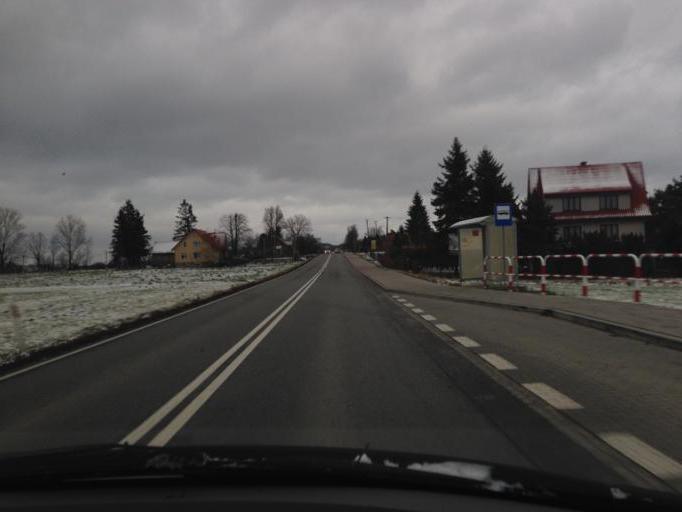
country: PL
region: Lesser Poland Voivodeship
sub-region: Powiat tarnowski
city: Zakliczyn
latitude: 49.8530
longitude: 20.8272
